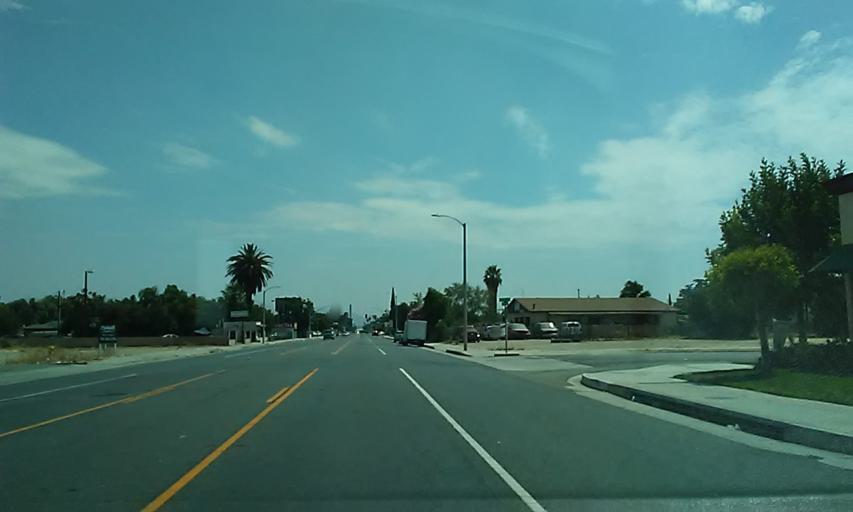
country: US
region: California
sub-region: San Bernardino County
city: San Bernardino
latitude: 34.1199
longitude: -117.3139
